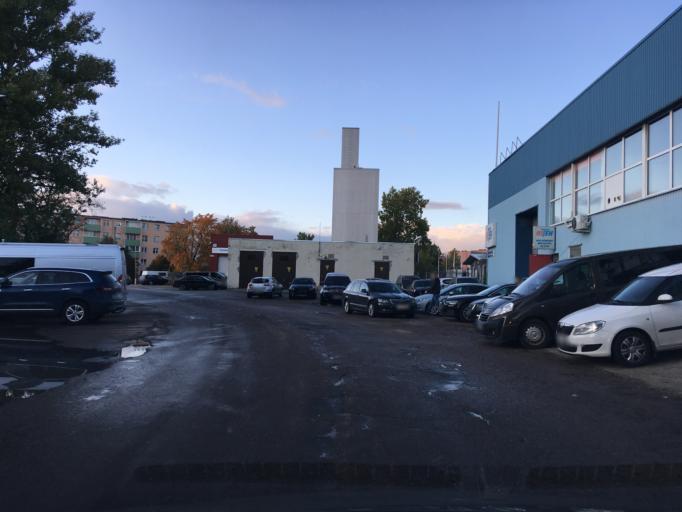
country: EE
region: Harju
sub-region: Tallinna linn
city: Tallinn
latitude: 59.4286
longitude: 24.8081
